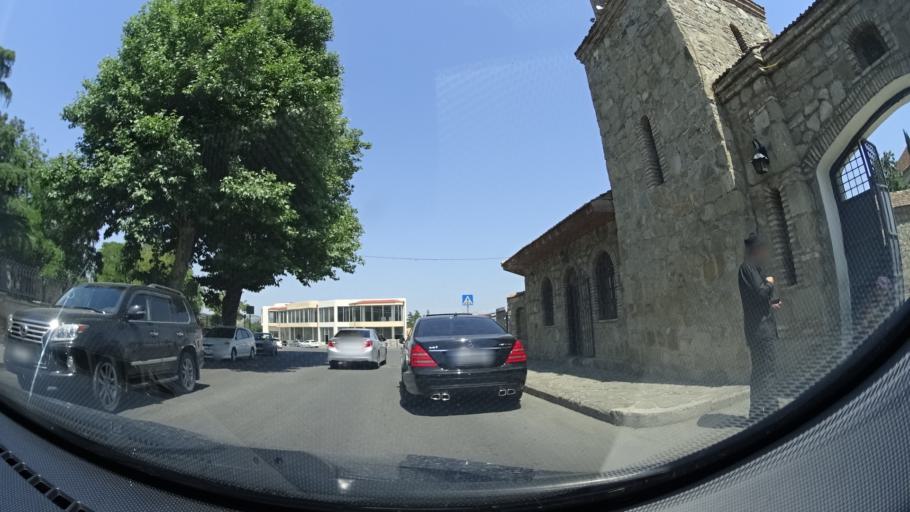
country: GE
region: Shida Kartli
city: Gori
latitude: 41.9866
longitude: 44.1117
